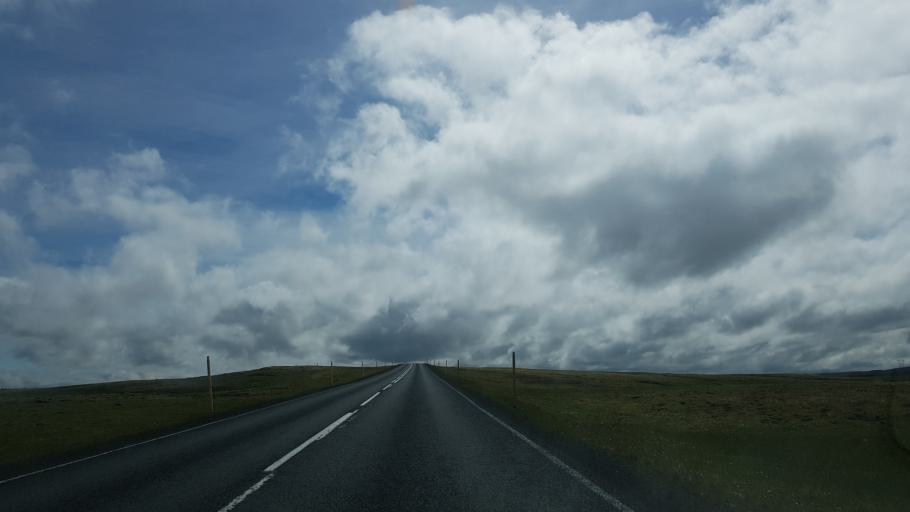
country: IS
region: West
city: Borgarnes
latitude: 65.0126
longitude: -21.0683
